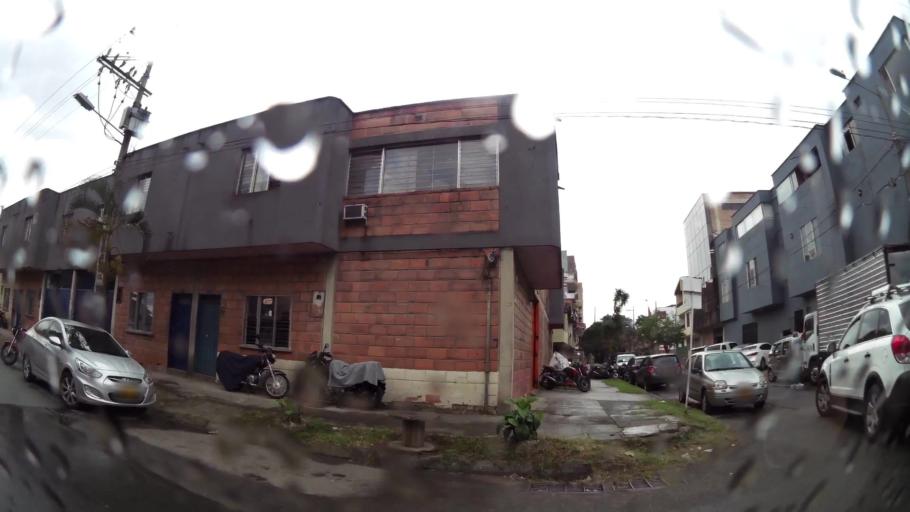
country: CO
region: Antioquia
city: Itagui
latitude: 6.1837
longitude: -75.5930
